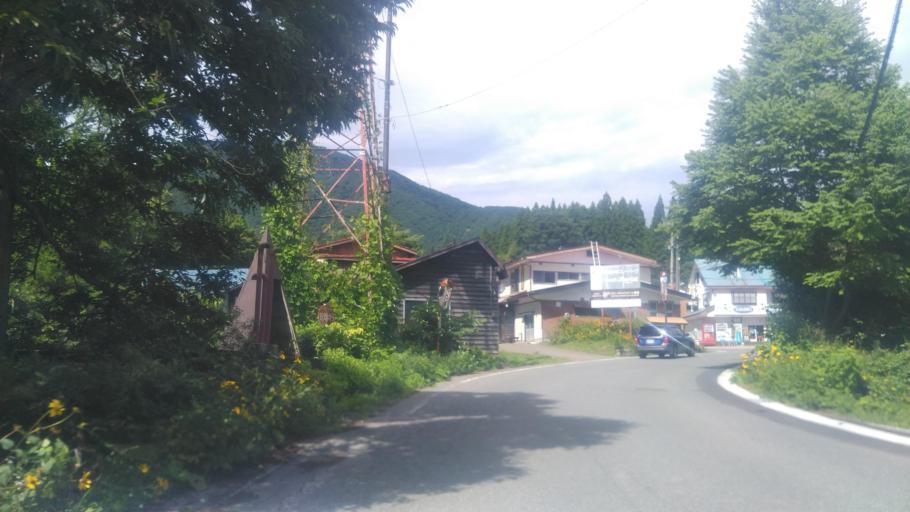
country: JP
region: Niigata
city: Arai
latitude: 36.8317
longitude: 138.1715
